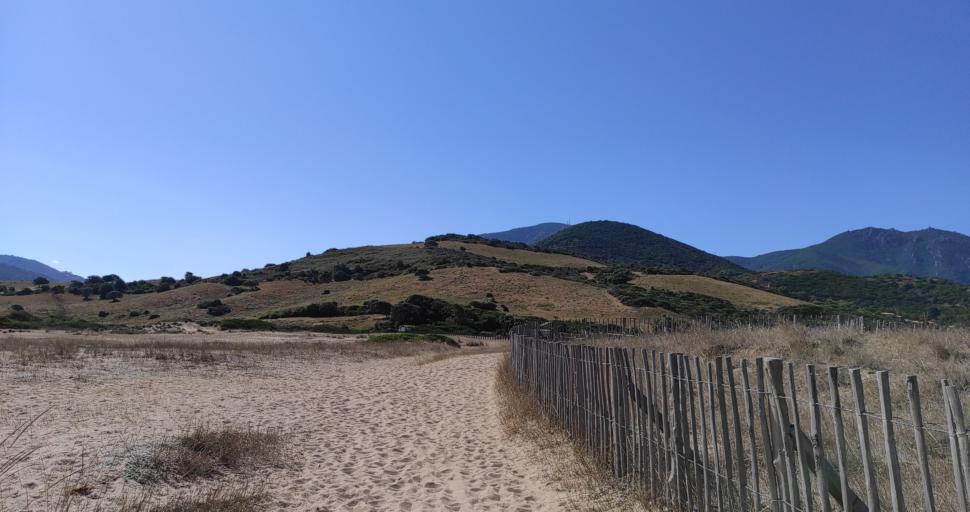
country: FR
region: Corsica
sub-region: Departement de la Corse-du-Sud
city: Alata
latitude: 41.9900
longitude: 8.6703
